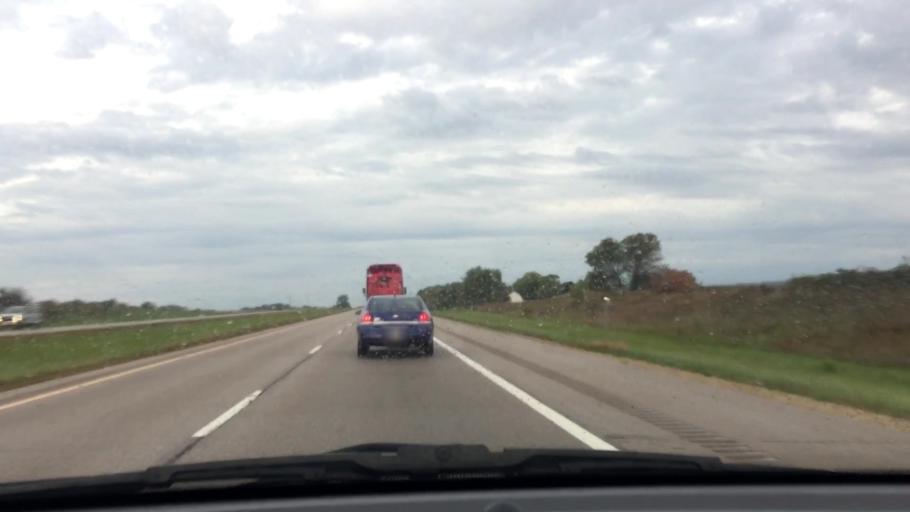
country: US
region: Wisconsin
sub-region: Rock County
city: Clinton
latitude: 42.5723
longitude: -88.8289
